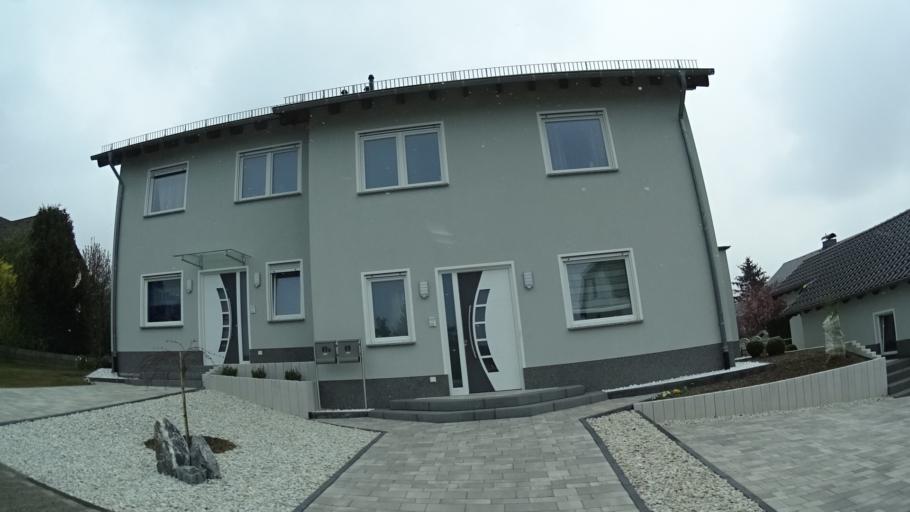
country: DE
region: Rheinland-Pfalz
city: Hintertiefenbach
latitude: 49.7261
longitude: 7.3352
